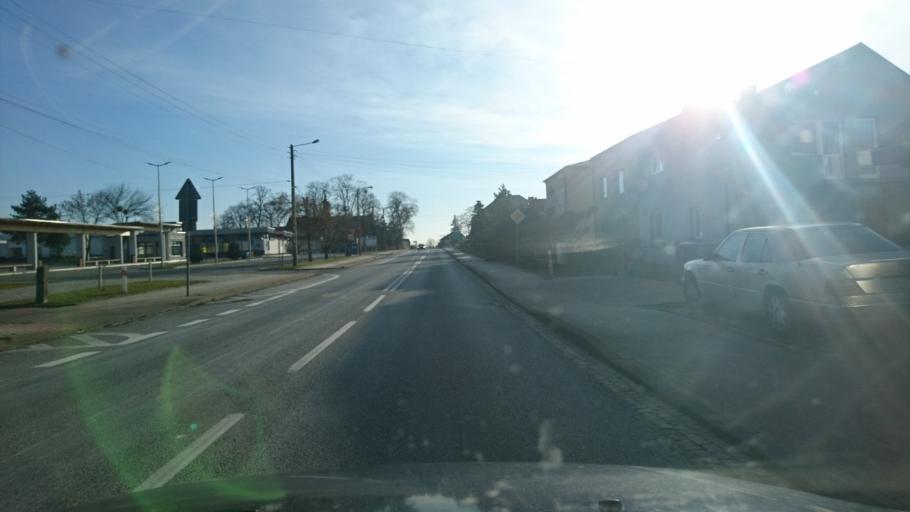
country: PL
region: Opole Voivodeship
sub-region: Powiat oleski
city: Dalachow
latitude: 51.0411
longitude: 18.5975
